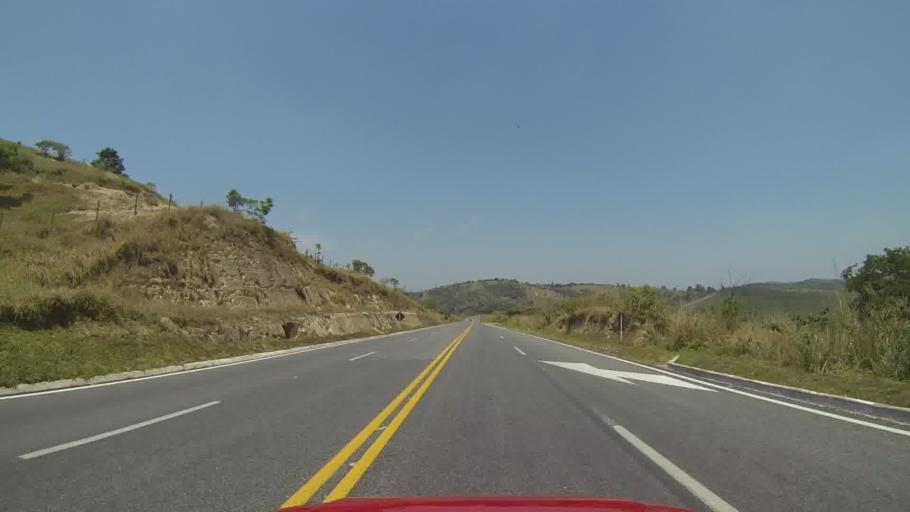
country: BR
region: Minas Gerais
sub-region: Itapecerica
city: Itapecerica
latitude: -20.2699
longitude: -45.1180
